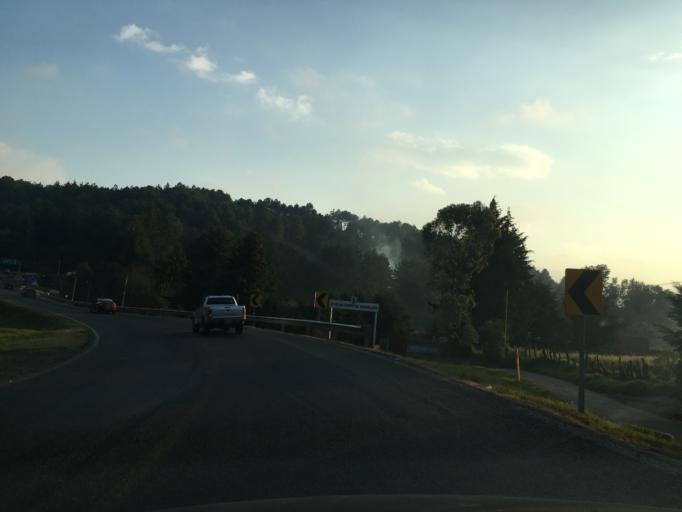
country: MX
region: Michoacan
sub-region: Patzcuaro
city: Santa Maria Huiramangaro (San Juan Tumbio)
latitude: 19.4848
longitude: -101.7406
